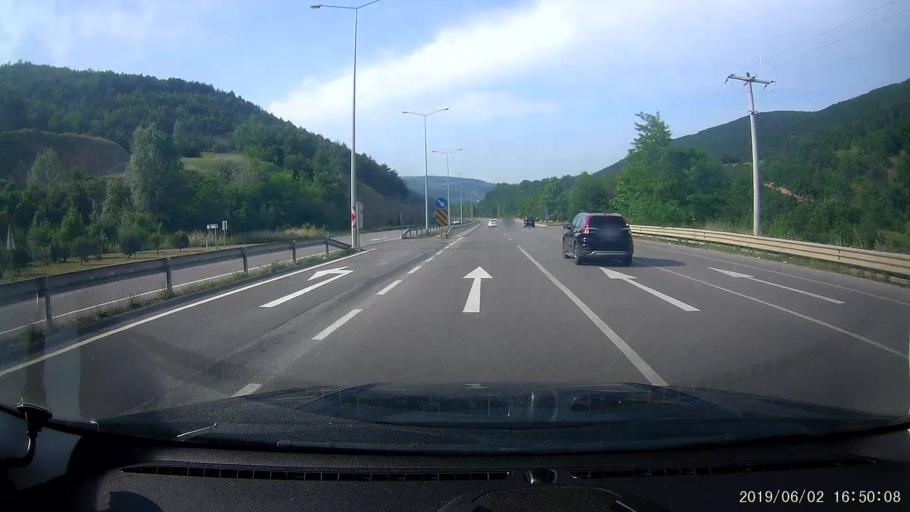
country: TR
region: Samsun
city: Samsun
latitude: 41.2482
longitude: 36.1731
